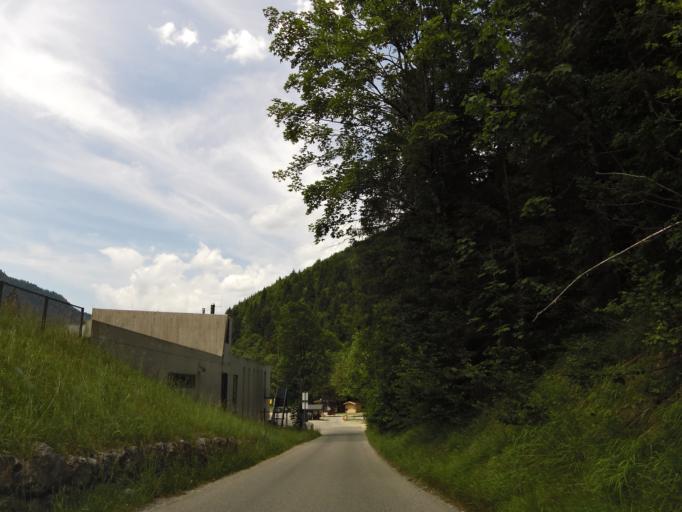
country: DE
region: Bavaria
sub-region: Upper Bavaria
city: Reit im Winkl
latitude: 47.6577
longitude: 12.5416
